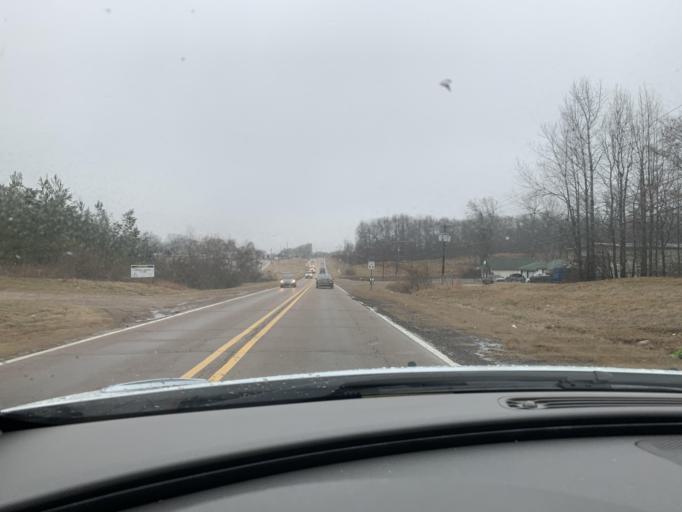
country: US
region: Mississippi
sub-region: De Soto County
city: Horn Lake
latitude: 34.8984
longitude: -89.9970
